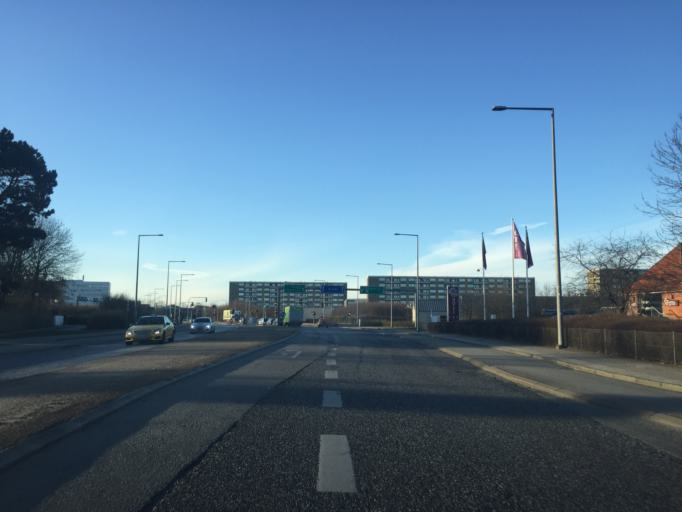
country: DK
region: Capital Region
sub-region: Tarnby Kommune
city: Tarnby
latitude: 55.6280
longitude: 12.6038
